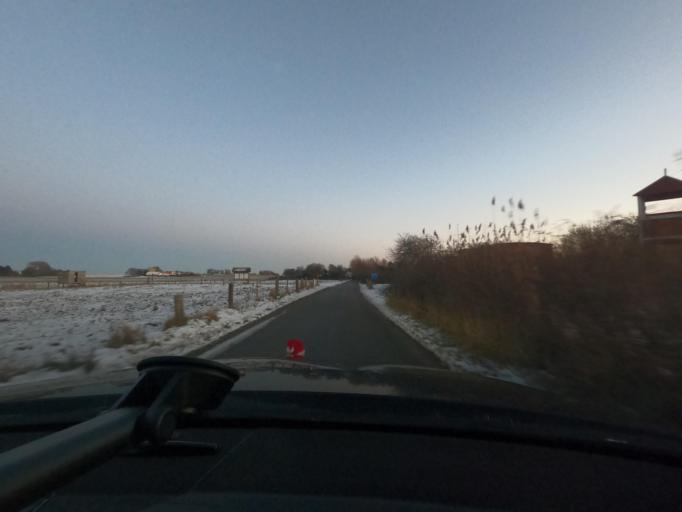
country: DK
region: South Denmark
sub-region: Sonderborg Kommune
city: Horuphav
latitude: 54.8639
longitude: 9.9135
